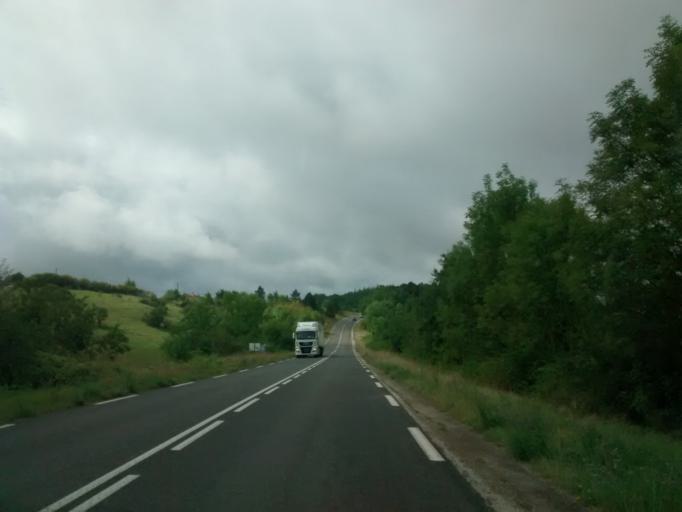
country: FR
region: Midi-Pyrenees
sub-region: Departement du Lot
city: Pradines
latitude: 44.5378
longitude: 1.4711
